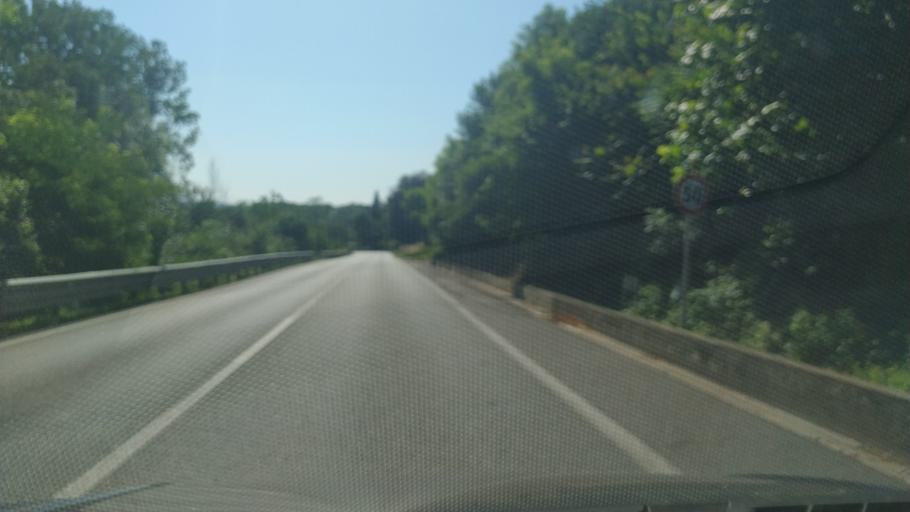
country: IT
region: Piedmont
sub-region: Provincia di Novara
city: Cureggio
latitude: 45.6687
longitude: 8.4490
